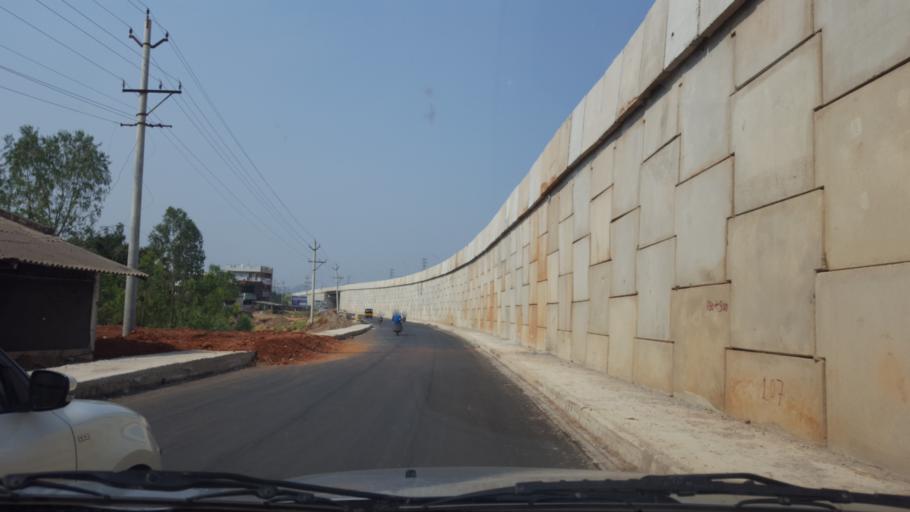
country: IN
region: Andhra Pradesh
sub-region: Vishakhapatnam
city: Vepagunta
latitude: 17.8784
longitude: 83.3072
